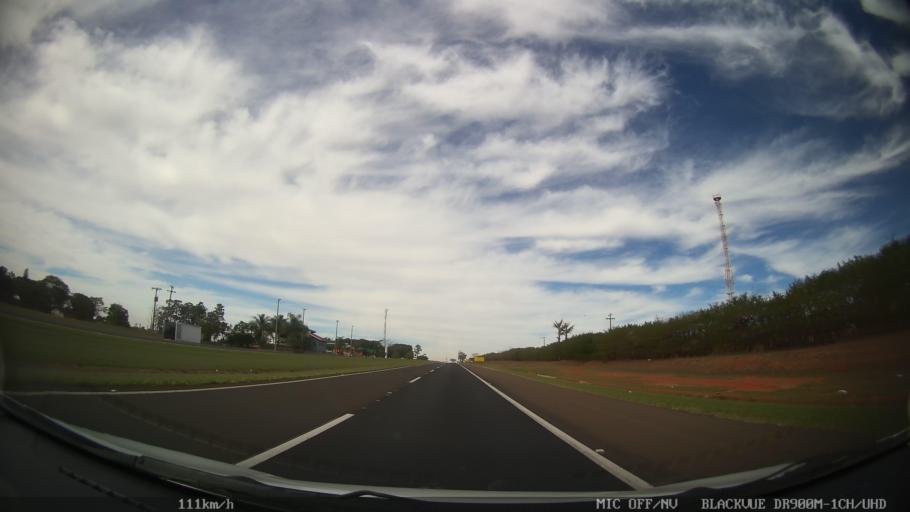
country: BR
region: Sao Paulo
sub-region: Taquaritinga
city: Taquaritinga
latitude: -21.4986
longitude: -48.5655
